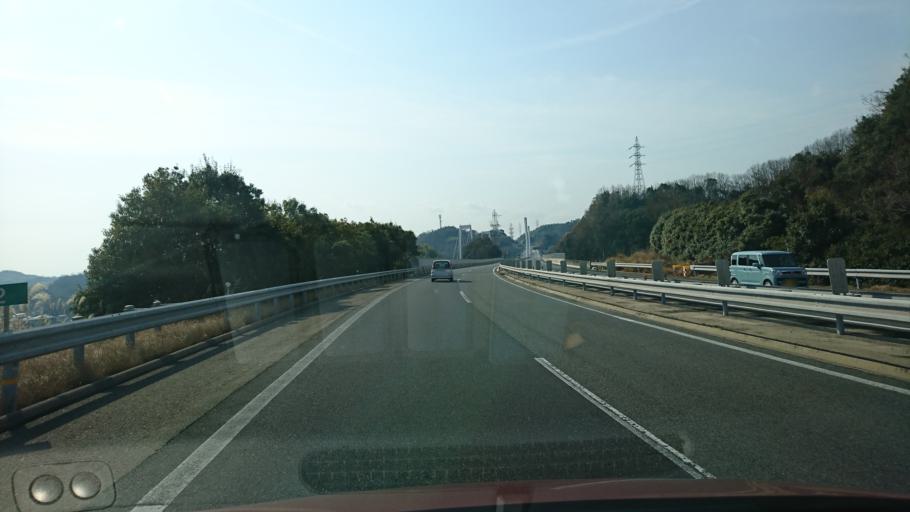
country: JP
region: Hiroshima
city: Onomichi
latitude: 34.4141
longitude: 133.2200
